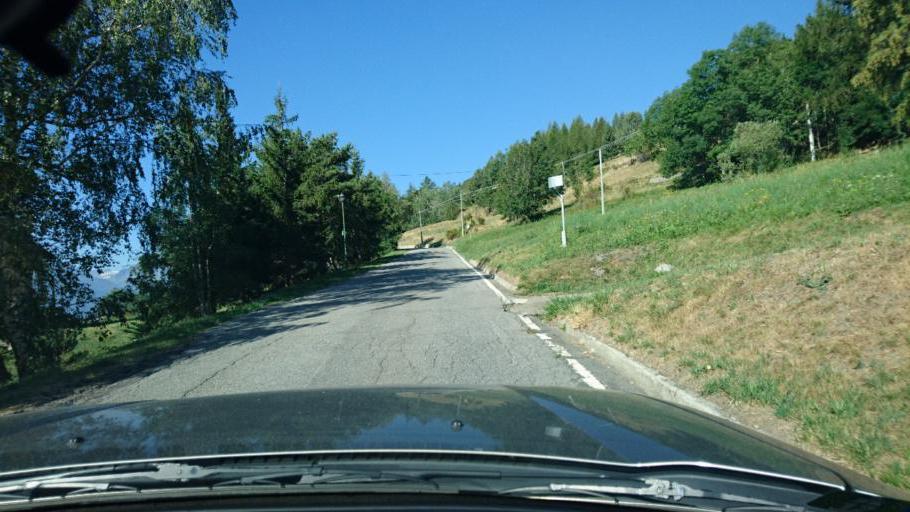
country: IT
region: Aosta Valley
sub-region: Valle d'Aosta
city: Villeneuve
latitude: 45.7283
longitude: 7.2024
